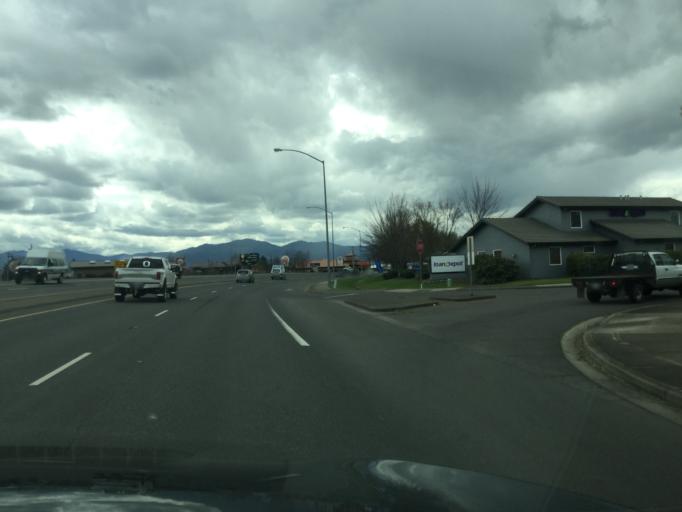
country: US
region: Oregon
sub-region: Jackson County
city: Medford
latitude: 42.3642
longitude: -122.8562
